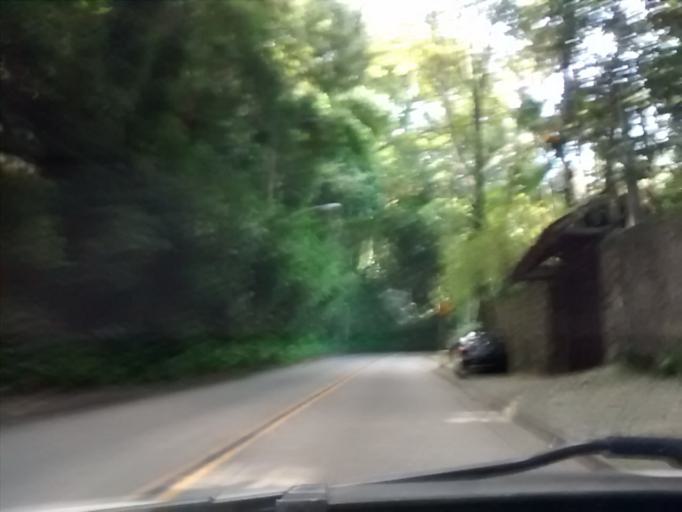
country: BR
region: Rio de Janeiro
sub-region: Rio De Janeiro
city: Rio de Janeiro
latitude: -22.9907
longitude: -43.2742
